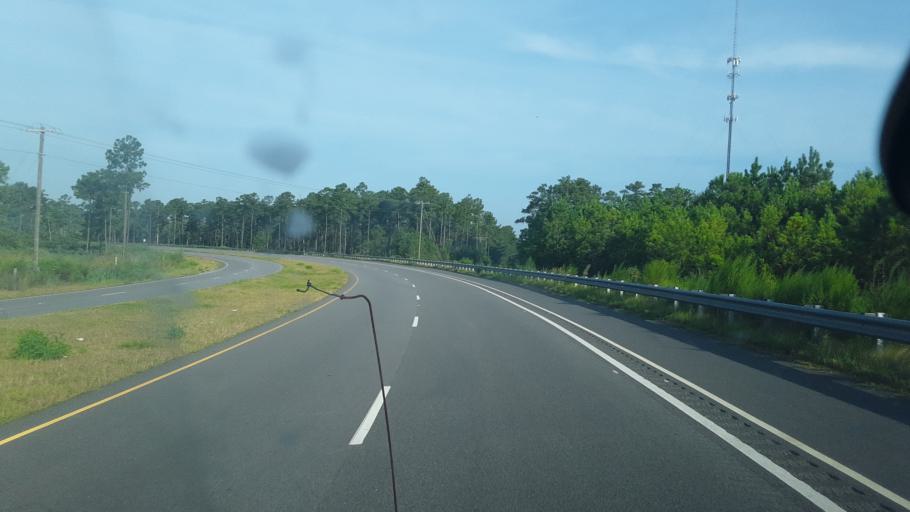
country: US
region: South Carolina
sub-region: Horry County
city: Forestbrook
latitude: 33.8167
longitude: -78.9045
